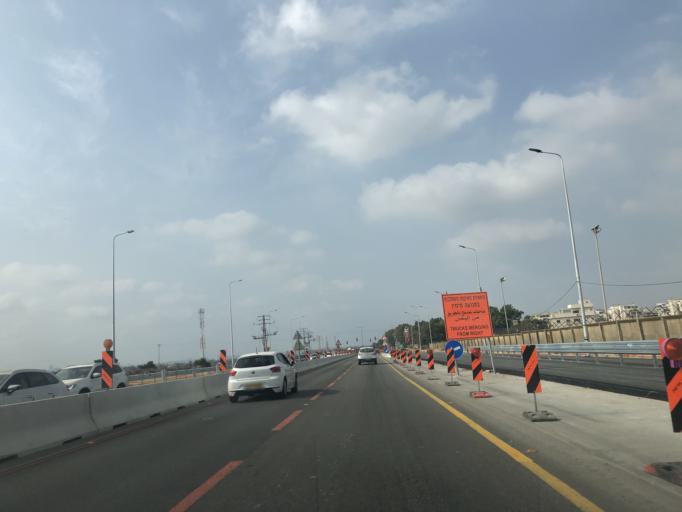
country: IL
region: Central District
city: Rosh Ha'Ayin
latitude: 32.0911
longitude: 34.9427
